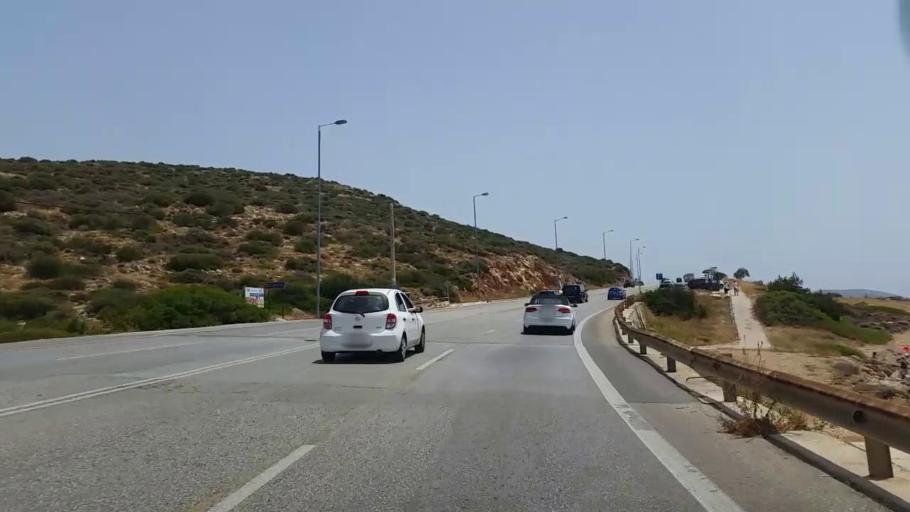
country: GR
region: Attica
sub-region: Nomarchia Anatolikis Attikis
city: Saronida
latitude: 37.7740
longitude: 23.9016
